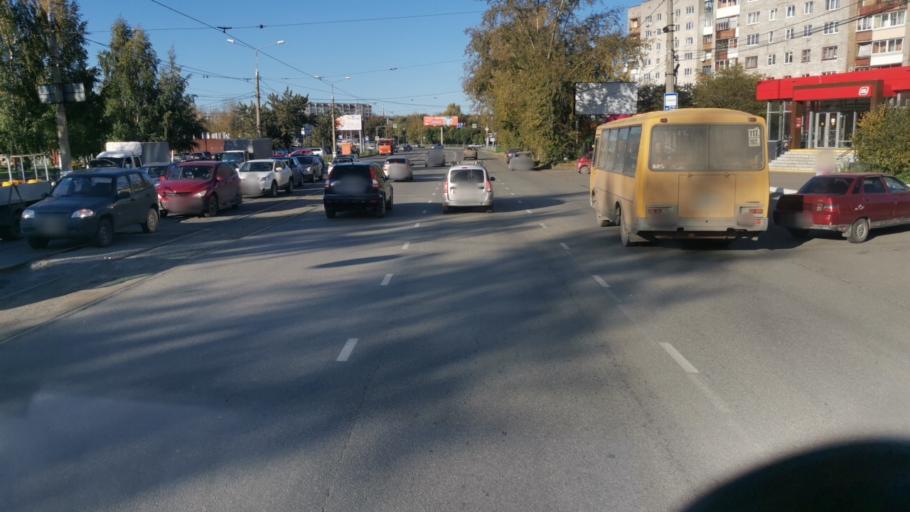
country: RU
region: Sverdlovsk
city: Nizhniy Tagil
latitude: 57.9107
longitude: 59.9475
